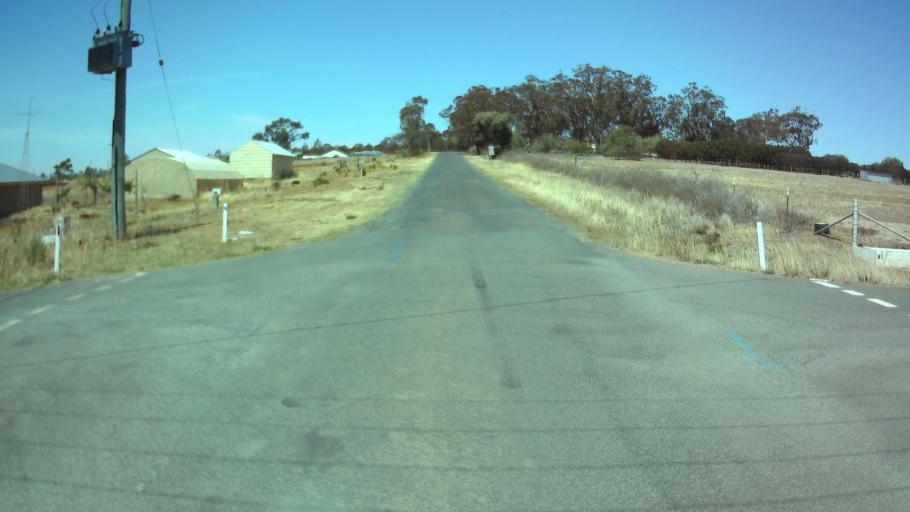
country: AU
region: New South Wales
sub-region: Weddin
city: Grenfell
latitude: -33.9001
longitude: 148.1727
